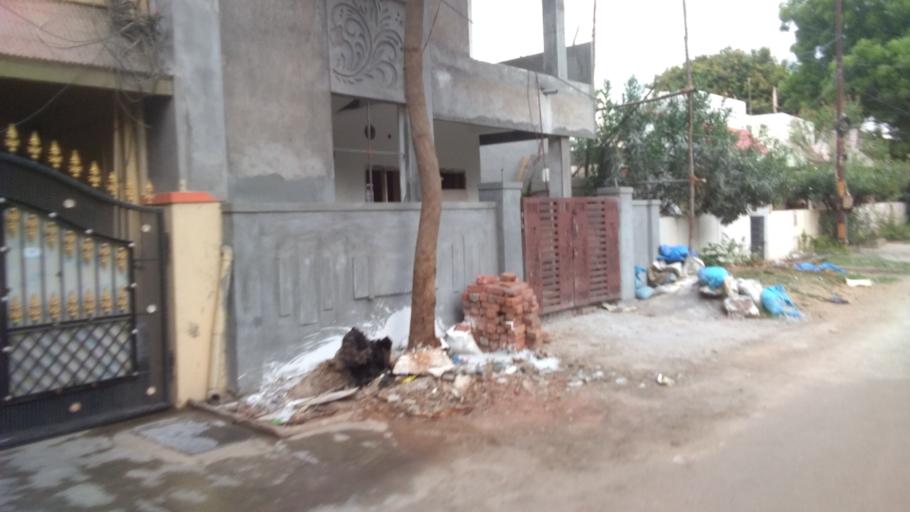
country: IN
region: Telangana
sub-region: Rangareddi
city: Gaddi Annaram
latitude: 17.3718
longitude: 78.5398
